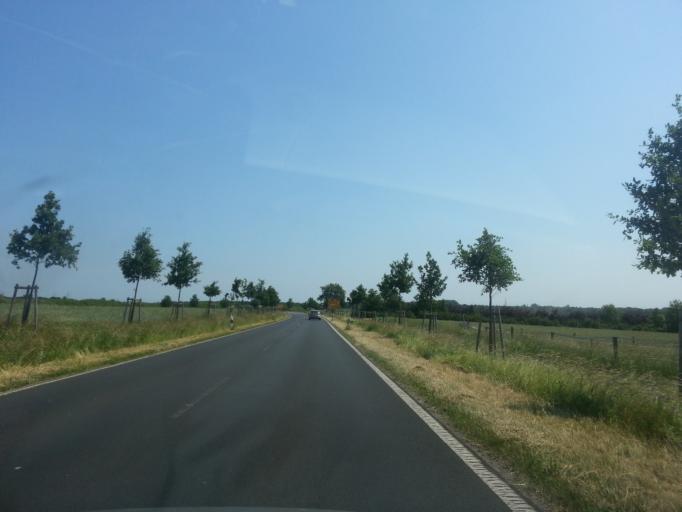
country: DE
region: Hesse
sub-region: Regierungsbezirk Darmstadt
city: Dietzenbach
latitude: 49.9988
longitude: 8.7388
